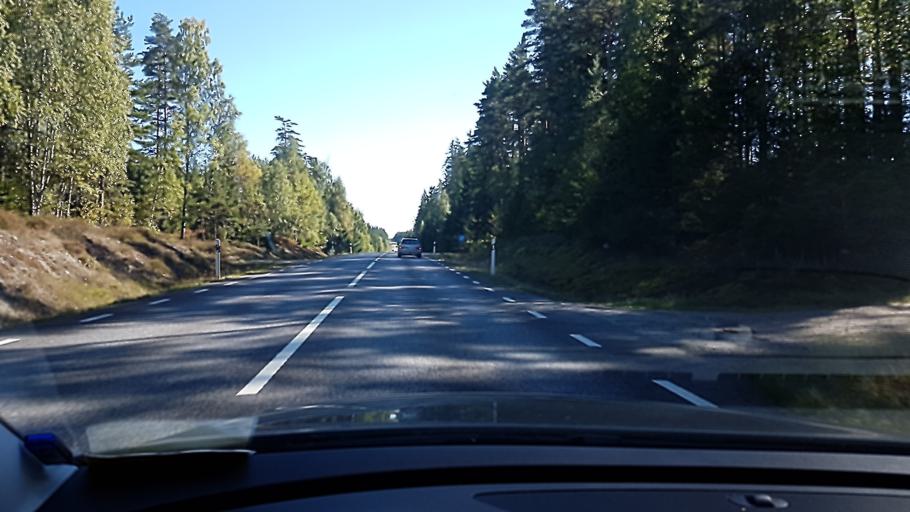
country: SE
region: Kronoberg
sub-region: Lessebo Kommun
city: Lessebo
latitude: 56.7320
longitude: 15.4122
